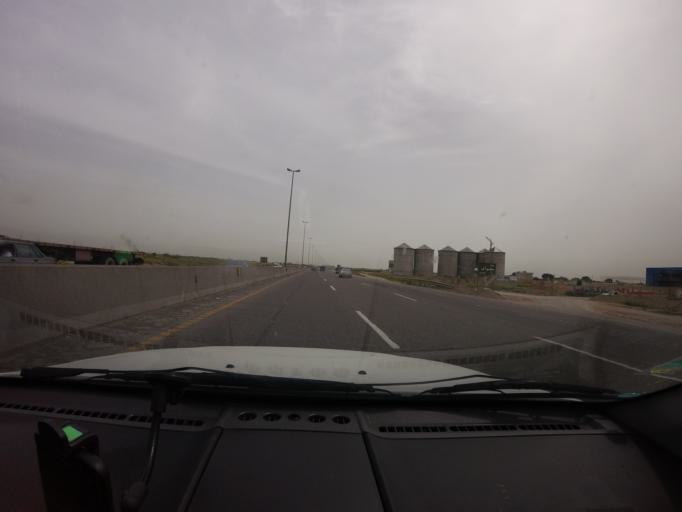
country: IR
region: Tehran
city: Robat Karim
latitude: 35.5289
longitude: 51.0897
